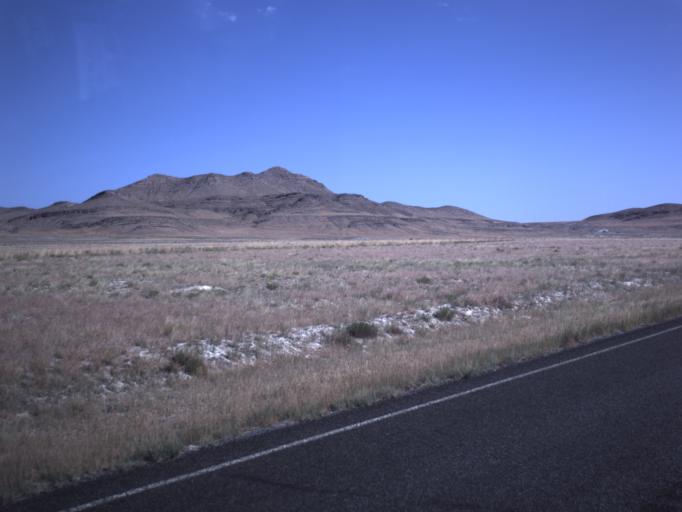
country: US
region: Utah
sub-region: Beaver County
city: Milford
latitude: 38.8481
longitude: -112.8431
